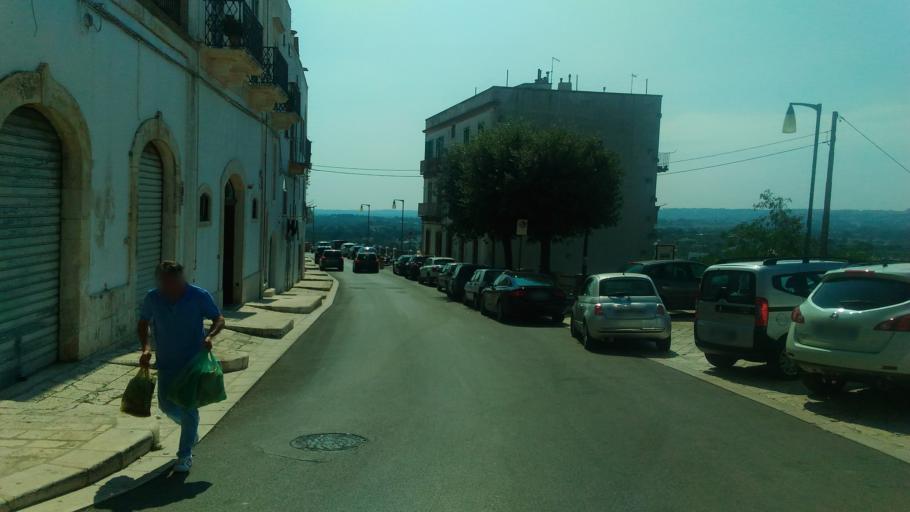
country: IT
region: Apulia
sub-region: Provincia di Bari
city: Locorotondo
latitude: 40.7527
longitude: 17.3283
